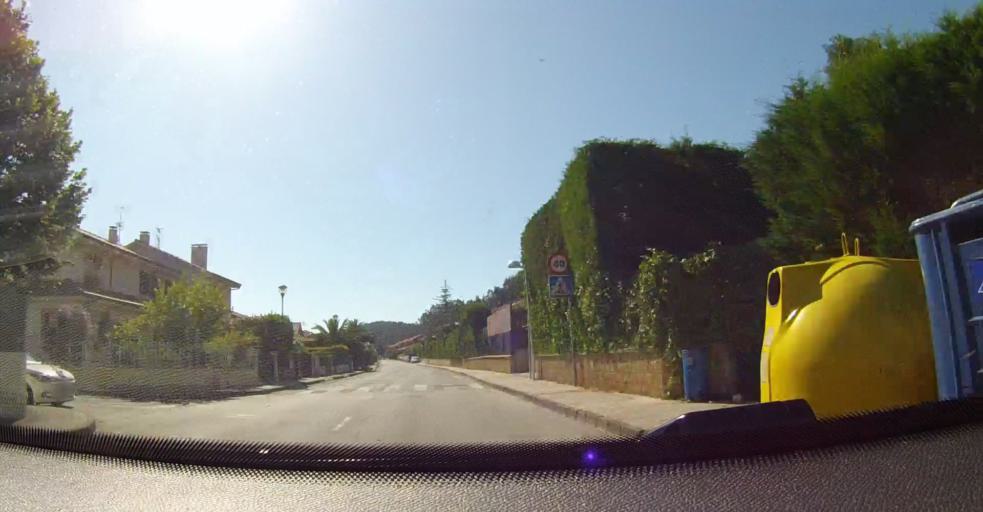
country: ES
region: Asturias
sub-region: Province of Asturias
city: Ribadesella
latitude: 43.4672
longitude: -5.0792
